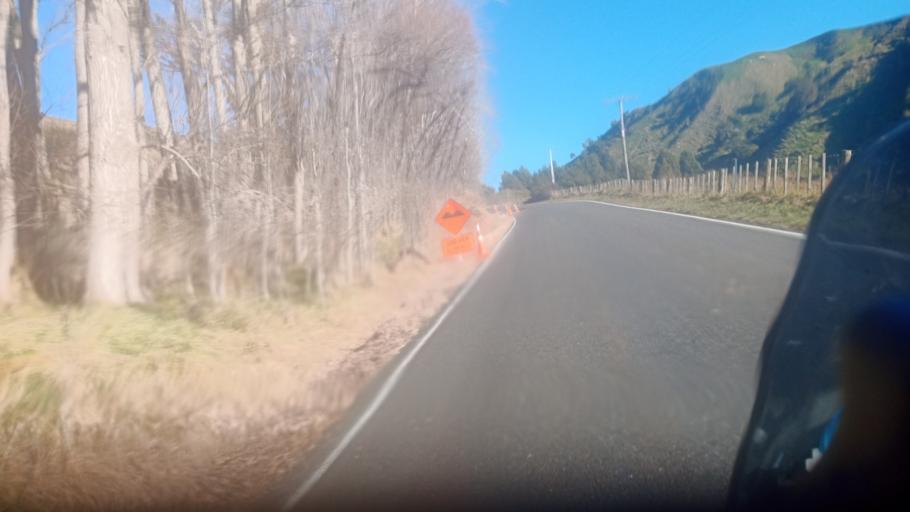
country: NZ
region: Gisborne
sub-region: Gisborne District
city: Gisborne
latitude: -38.5641
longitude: 177.6084
